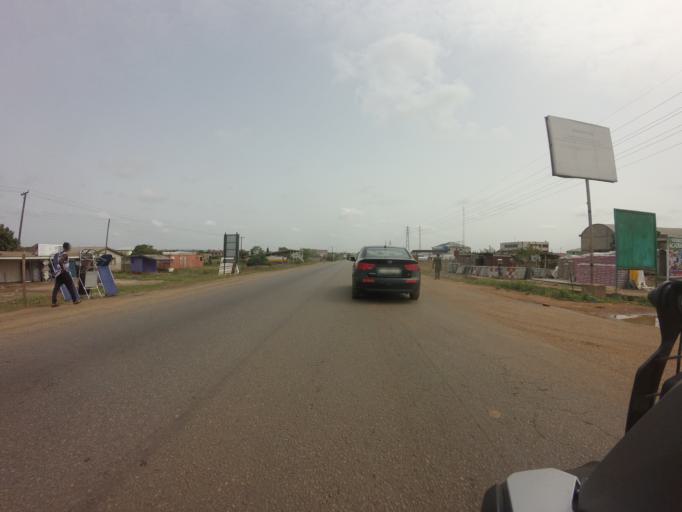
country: GH
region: Greater Accra
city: Tema
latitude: 5.7401
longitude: 0.0345
